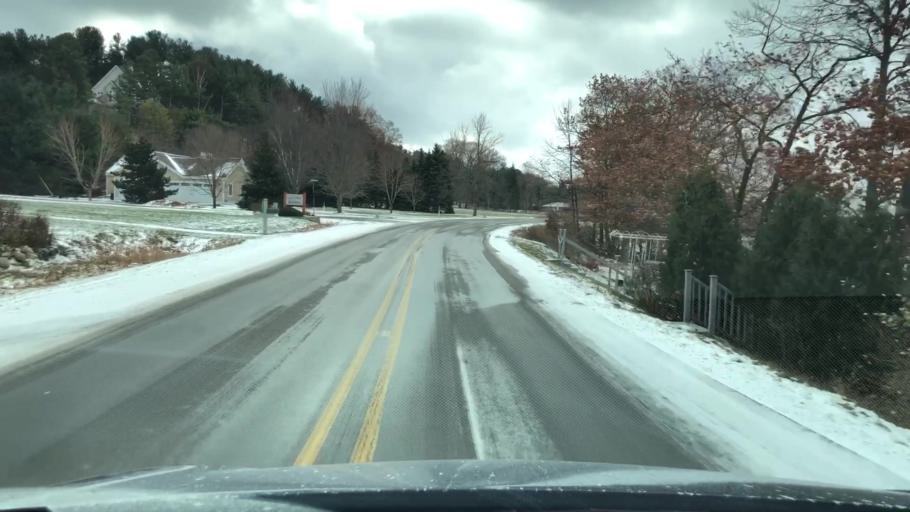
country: US
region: Michigan
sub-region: Leelanau County
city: Greilickville
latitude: 44.8519
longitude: -85.5545
